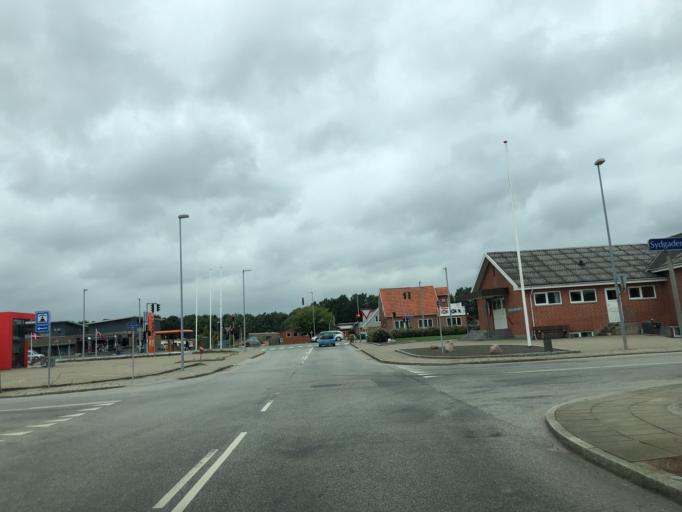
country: DK
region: Central Jutland
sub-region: Herning Kommune
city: Snejbjerg
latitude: 56.1317
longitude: 8.8996
